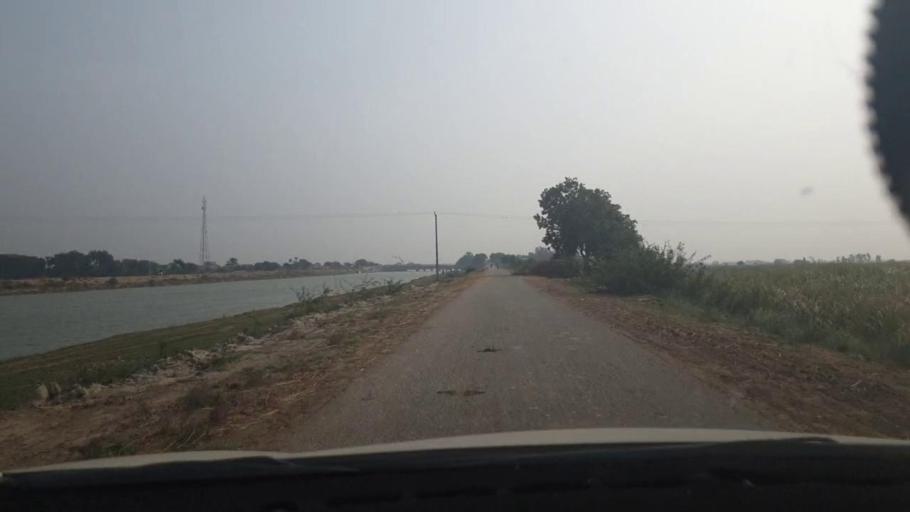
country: PK
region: Sindh
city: Tando Muhammad Khan
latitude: 24.9630
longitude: 68.4956
